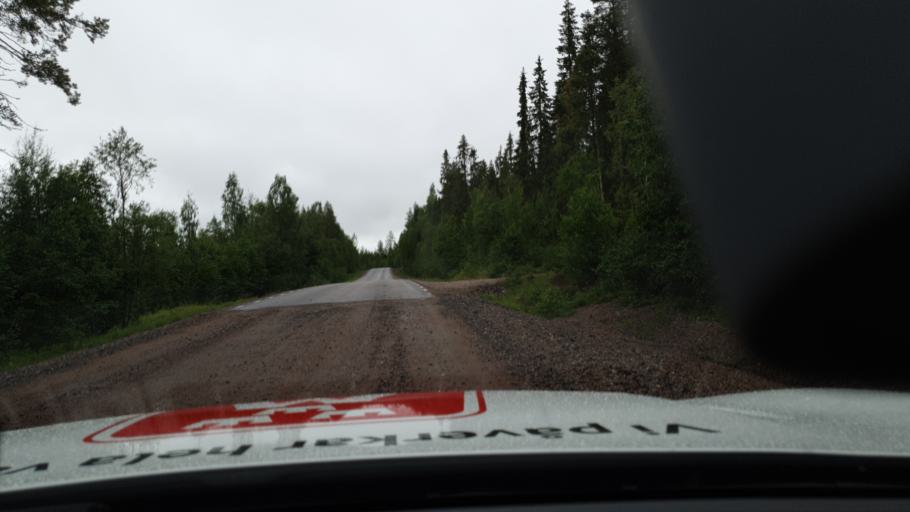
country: SE
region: Norrbotten
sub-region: Overtornea Kommun
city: OEvertornea
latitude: 66.4233
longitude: 23.5441
